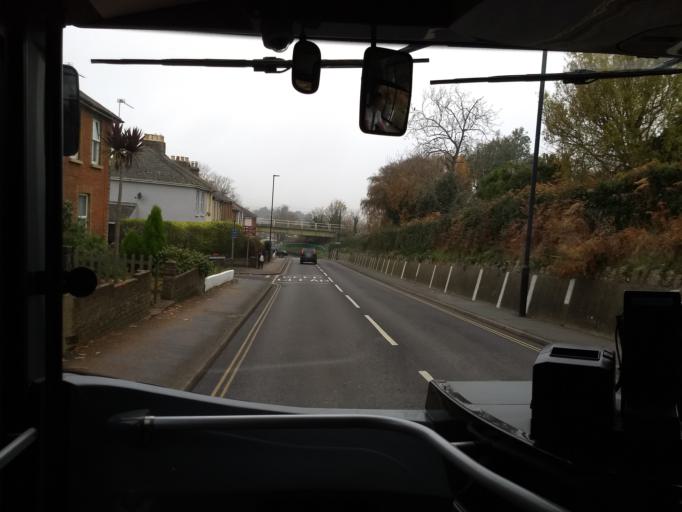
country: GB
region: England
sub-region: Isle of Wight
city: Sandown
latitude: 50.6503
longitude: -1.1640
